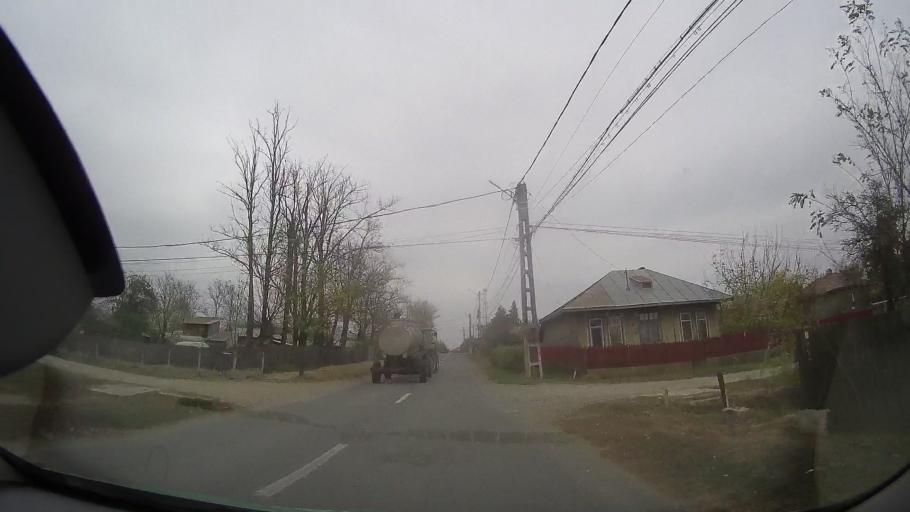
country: RO
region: Ialomita
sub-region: Comuna Grindu
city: Grindu
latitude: 44.7727
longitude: 26.9092
